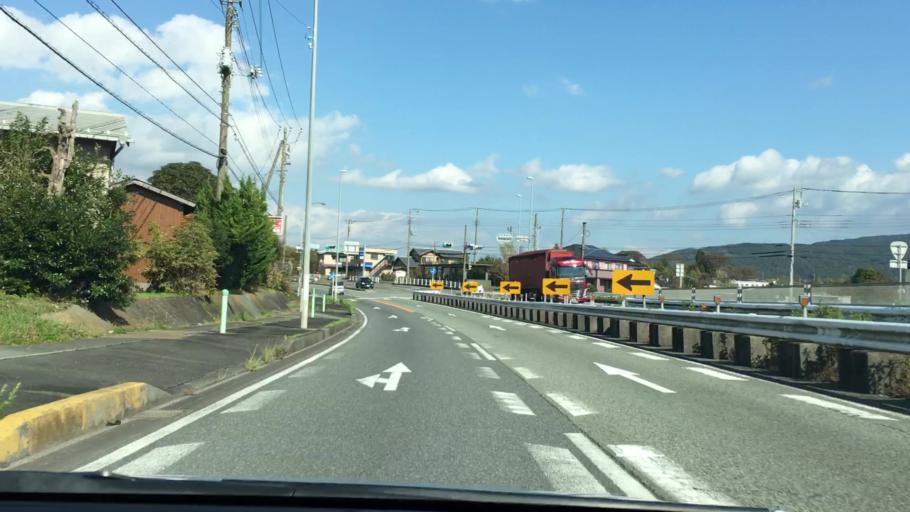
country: JP
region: Shizuoka
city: Gotemba
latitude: 35.2548
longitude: 138.9123
